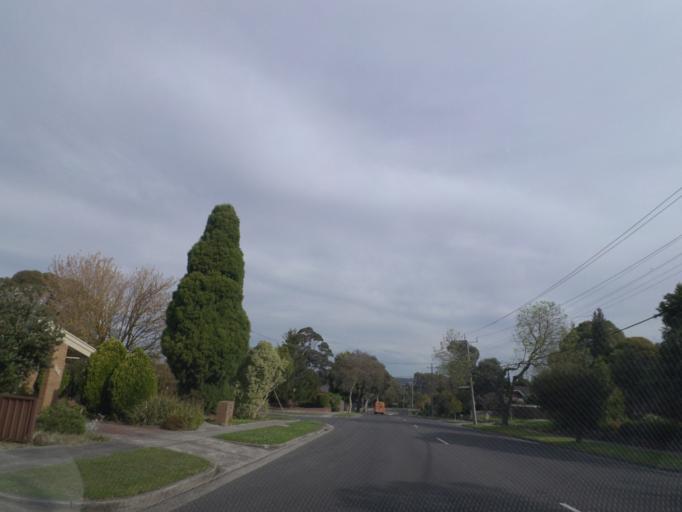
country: AU
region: Victoria
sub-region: Whitehorse
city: Vermont
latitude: -37.8490
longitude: 145.1966
